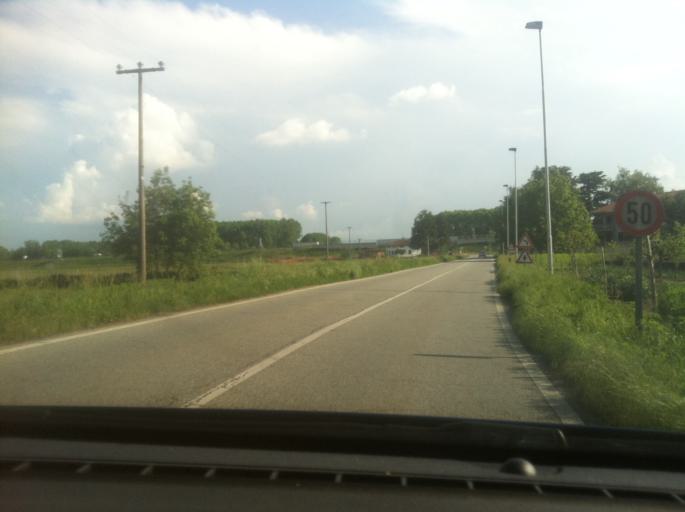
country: IT
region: Piedmont
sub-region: Provincia di Torino
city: Pavone Canavese
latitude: 45.4275
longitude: 7.8589
